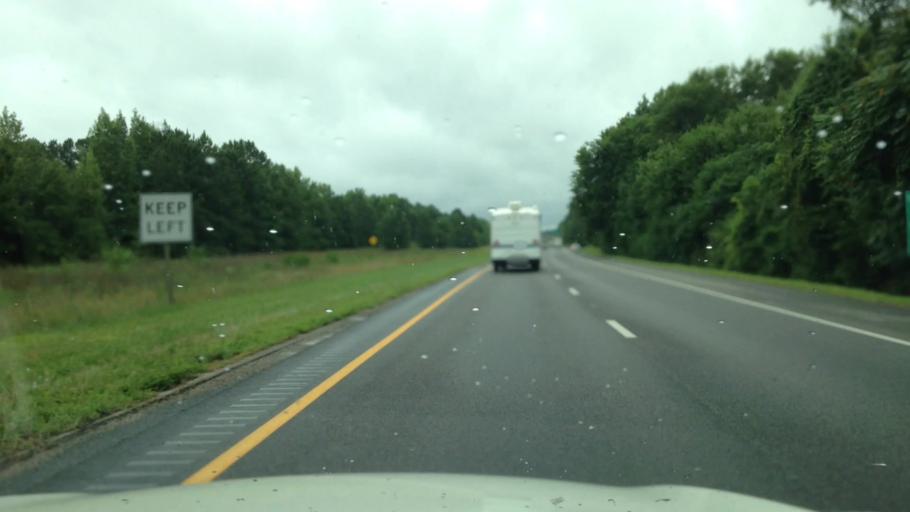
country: US
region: Virginia
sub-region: City of Petersburg
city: Petersburg
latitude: 37.1645
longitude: -77.3511
